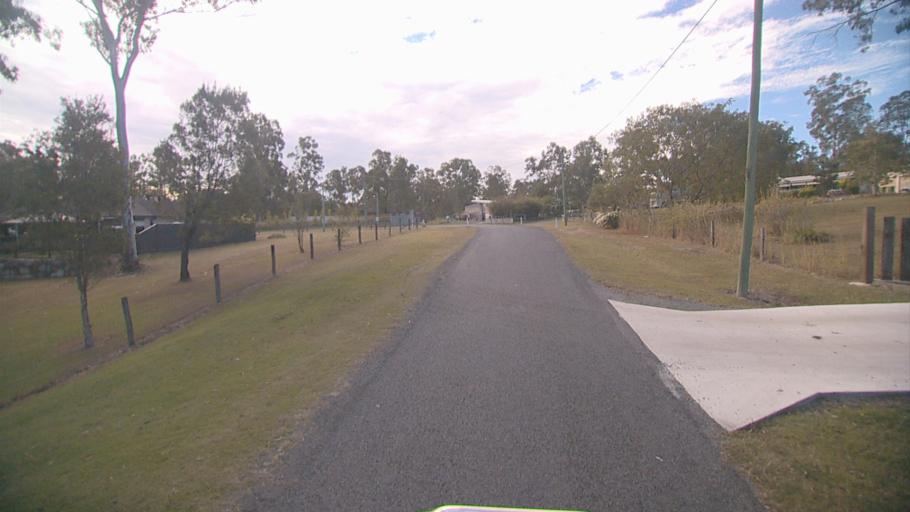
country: AU
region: Queensland
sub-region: Logan
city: North Maclean
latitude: -27.8210
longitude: 153.0490
